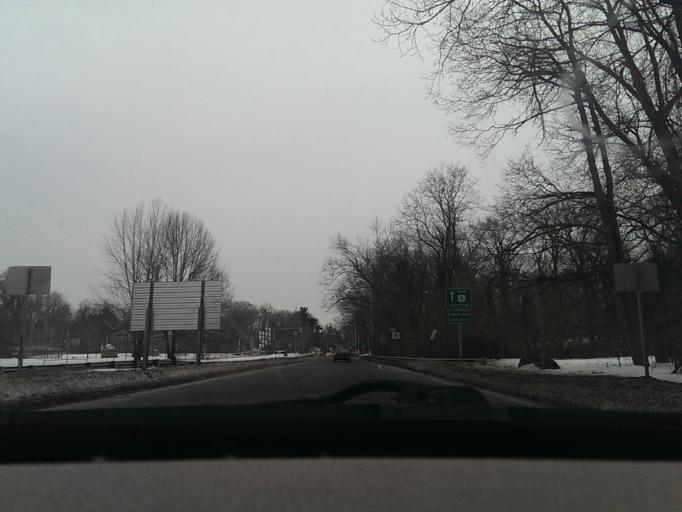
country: US
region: Massachusetts
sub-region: Hampden County
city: Longmeadow
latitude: 42.0735
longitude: -72.5828
